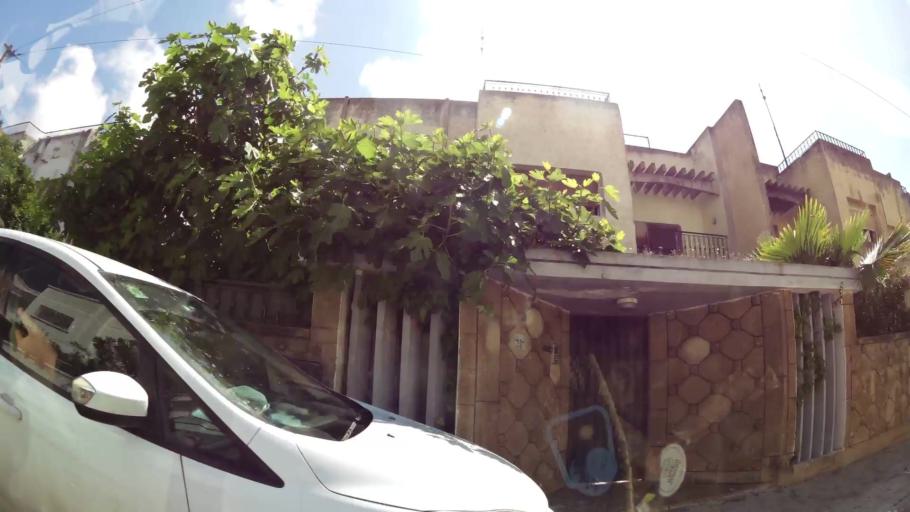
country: MA
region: Rabat-Sale-Zemmour-Zaer
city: Sale
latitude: 34.0360
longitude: -6.7940
